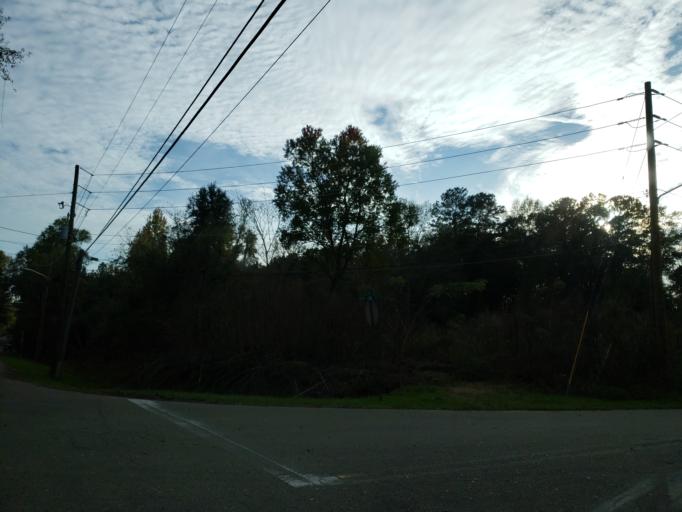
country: US
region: Mississippi
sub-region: Forrest County
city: Hattiesburg
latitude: 31.2964
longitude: -89.2843
